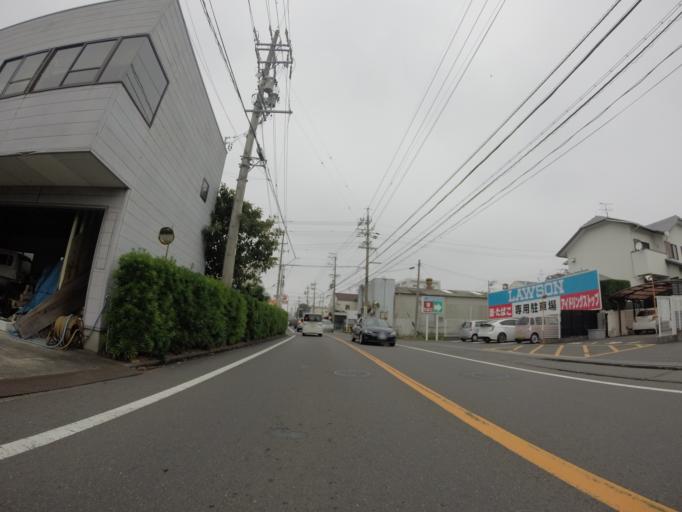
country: JP
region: Shizuoka
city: Shizuoka-shi
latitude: 34.9527
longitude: 138.3948
